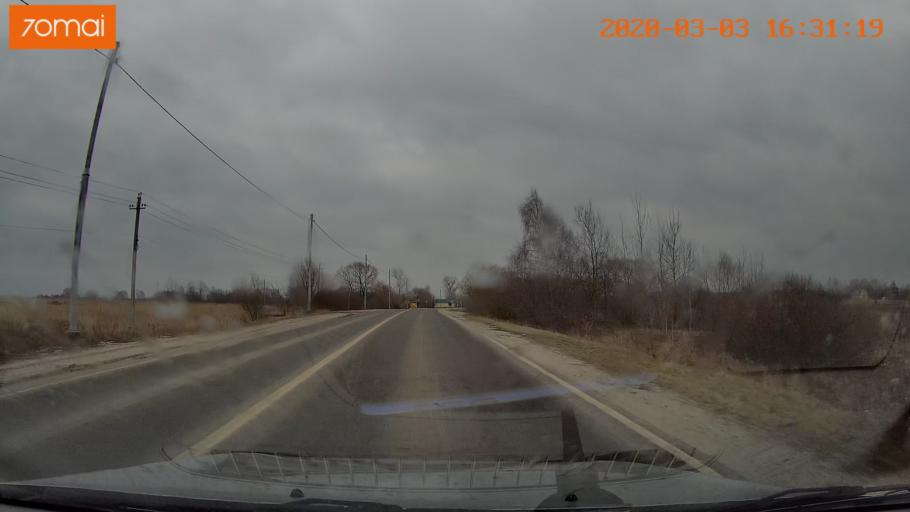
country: RU
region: Moskovskaya
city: Konobeyevo
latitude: 55.4261
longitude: 38.7237
